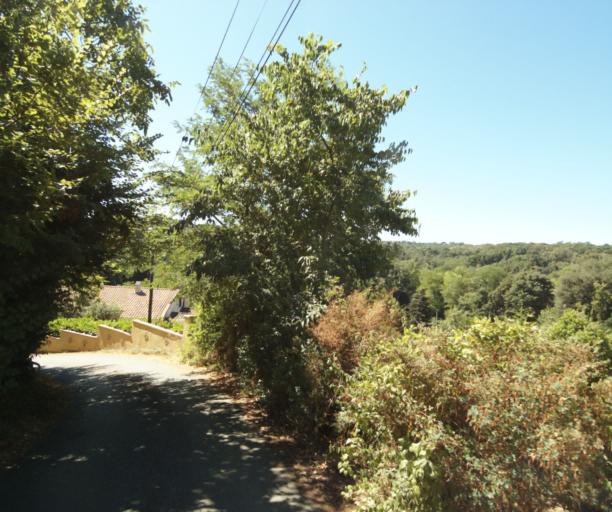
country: FR
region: Midi-Pyrenees
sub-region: Departement de la Haute-Garonne
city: Castanet-Tolosan
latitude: 43.5159
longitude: 1.4867
